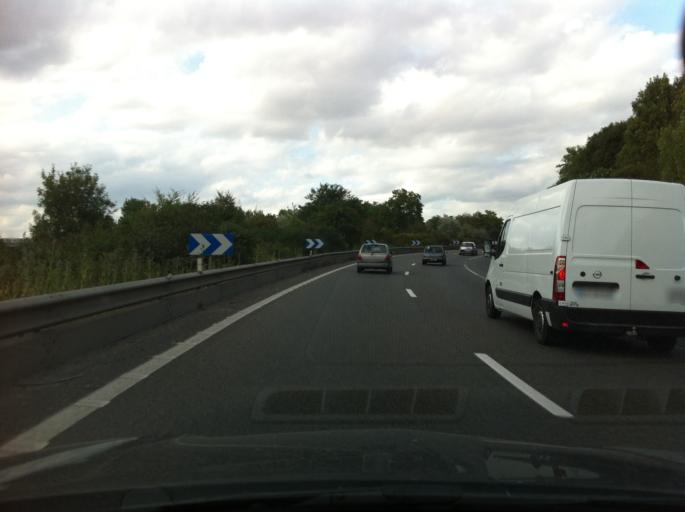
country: FR
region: Ile-de-France
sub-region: Departement de Seine-et-Marne
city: Lieusaint
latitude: 48.6424
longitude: 2.5356
